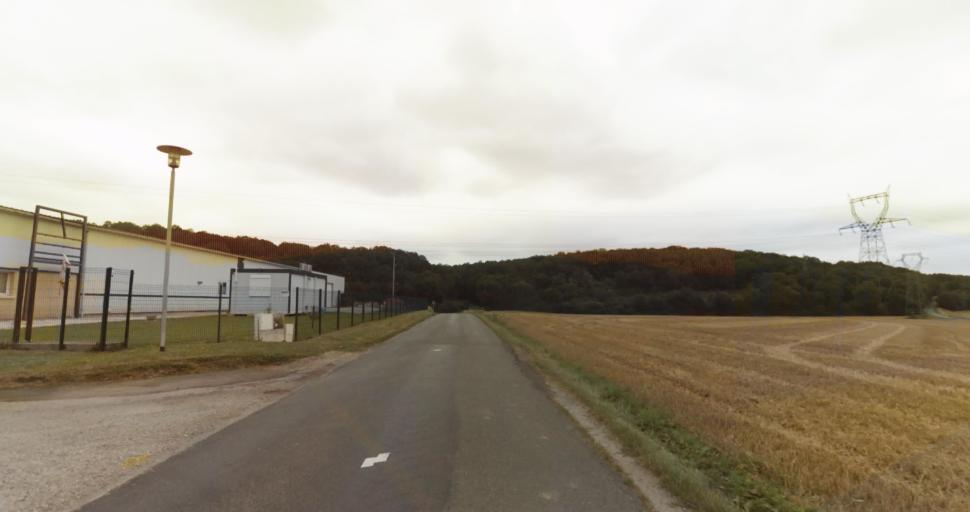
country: FR
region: Haute-Normandie
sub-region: Departement de l'Eure
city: Croth
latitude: 48.8770
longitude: 1.3692
